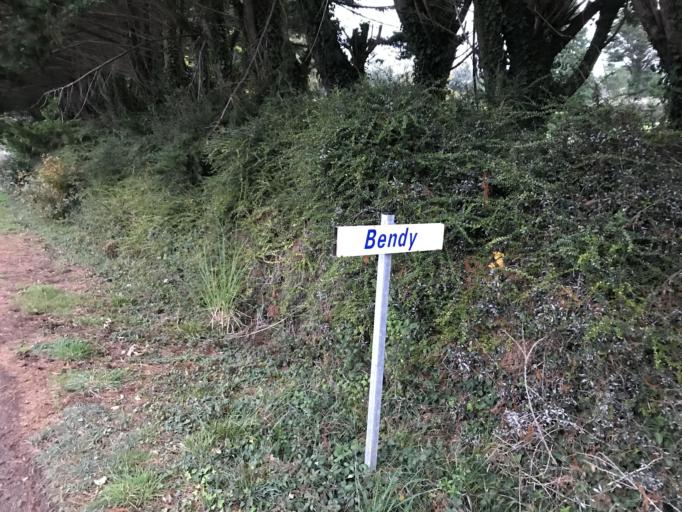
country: FR
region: Brittany
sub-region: Departement du Finistere
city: Logonna-Daoulas
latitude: 48.3158
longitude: -4.3300
